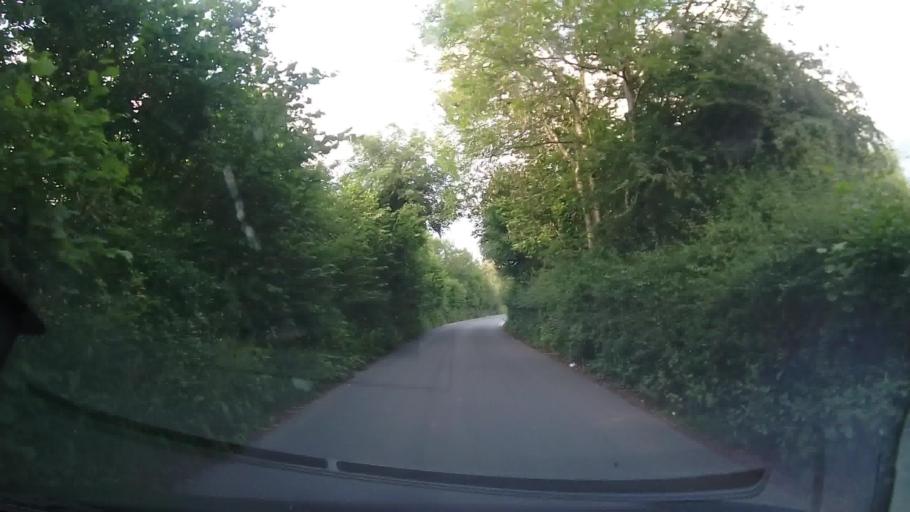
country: GB
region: Wales
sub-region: Gwynedd
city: Bala
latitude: 52.9012
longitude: -3.5958
